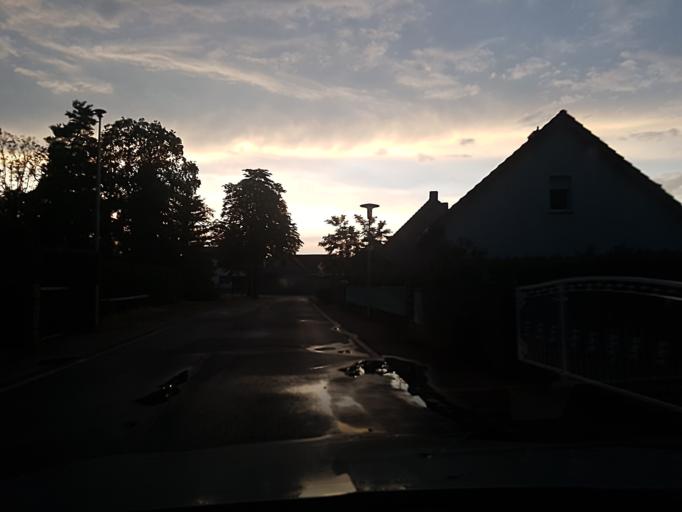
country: DE
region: Brandenburg
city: Bad Liebenwerda
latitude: 51.4997
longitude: 13.4265
